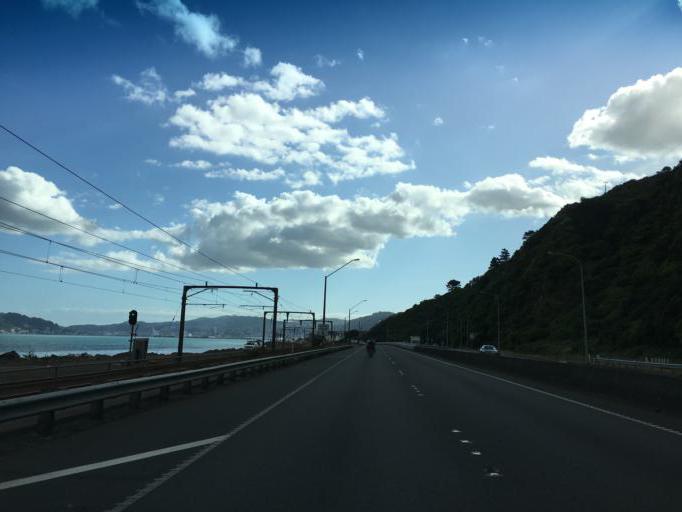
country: NZ
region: Wellington
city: Petone
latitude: -41.2425
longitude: 174.8217
